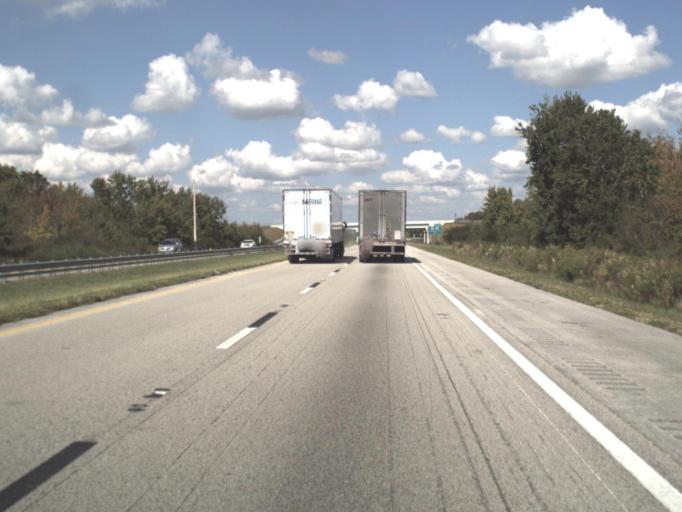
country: US
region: Florida
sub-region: Indian River County
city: Fellsmere
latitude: 27.6917
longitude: -80.8949
